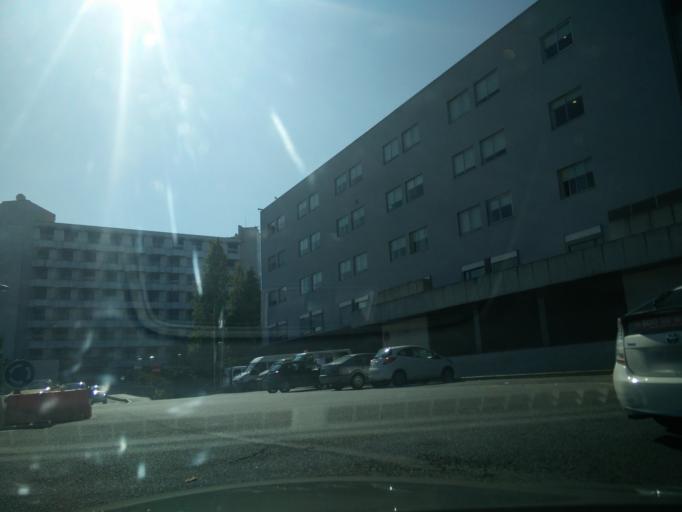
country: ES
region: Galicia
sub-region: Provincia da Coruna
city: A Coruna
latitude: 43.3440
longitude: -8.3877
